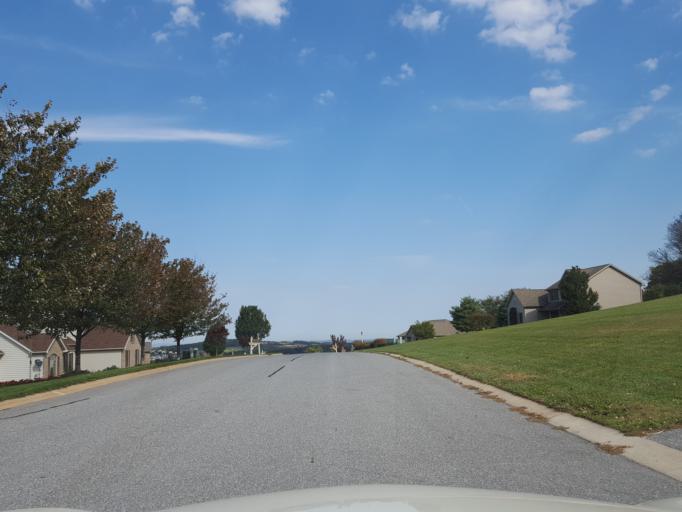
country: US
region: Pennsylvania
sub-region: York County
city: Yoe
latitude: 39.9138
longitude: -76.6236
